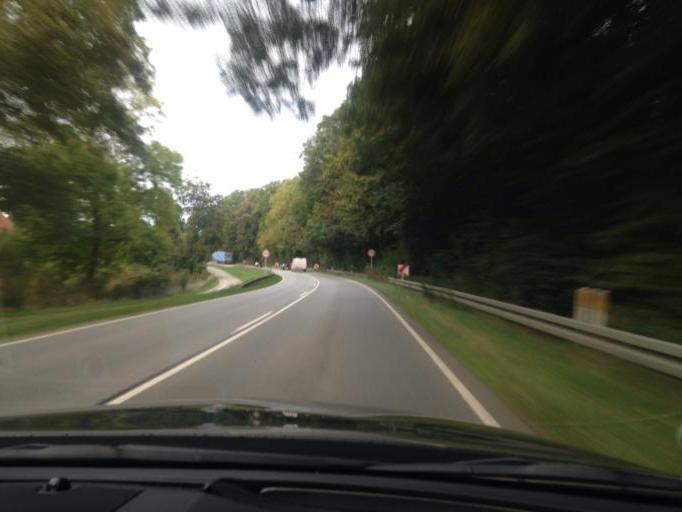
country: DK
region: South Denmark
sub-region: Haderslev Kommune
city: Vojens
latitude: 55.2563
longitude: 9.3325
